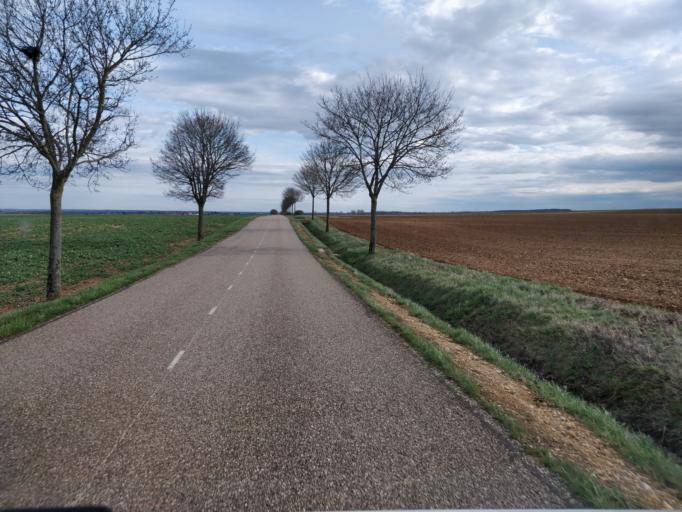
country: FR
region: Lorraine
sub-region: Departement de Meurthe-et-Moselle
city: Doncourt-les-Conflans
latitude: 49.1165
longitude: 5.9077
